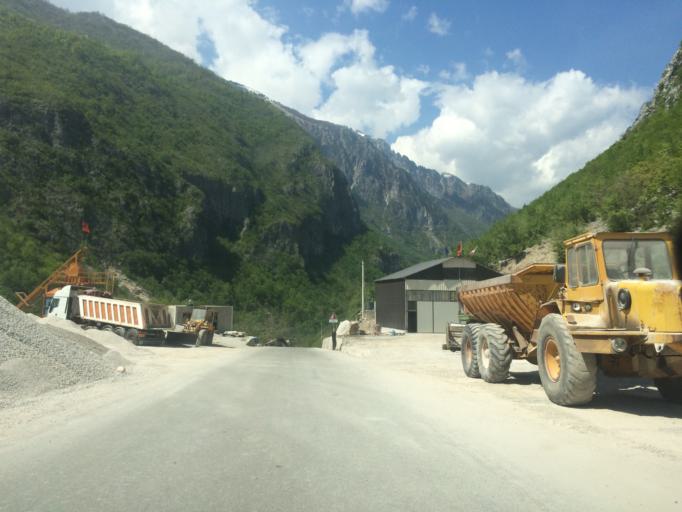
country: AL
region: Kukes
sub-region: Rrethi i Tropojes
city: Bajram Curri
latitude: 42.3913
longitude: 20.0705
